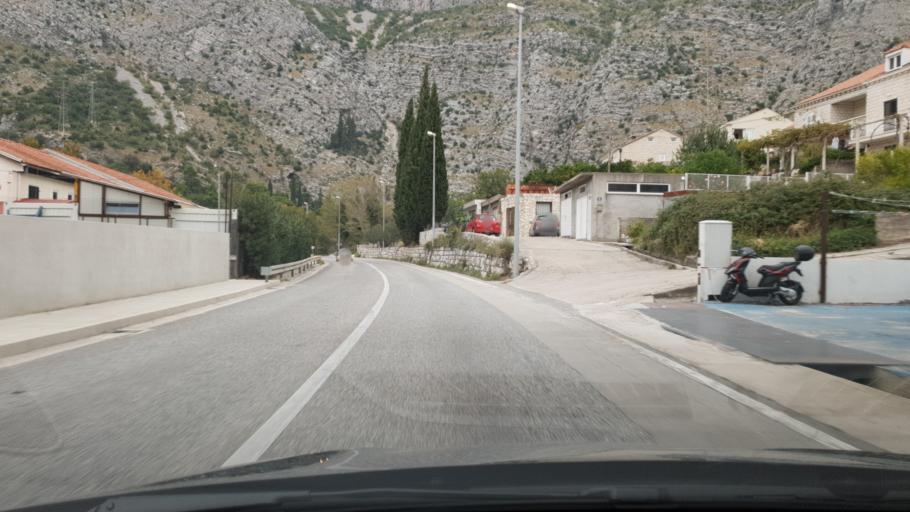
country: HR
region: Dubrovacko-Neretvanska
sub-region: Grad Dubrovnik
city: Mokosica
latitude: 42.6720
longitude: 18.1360
